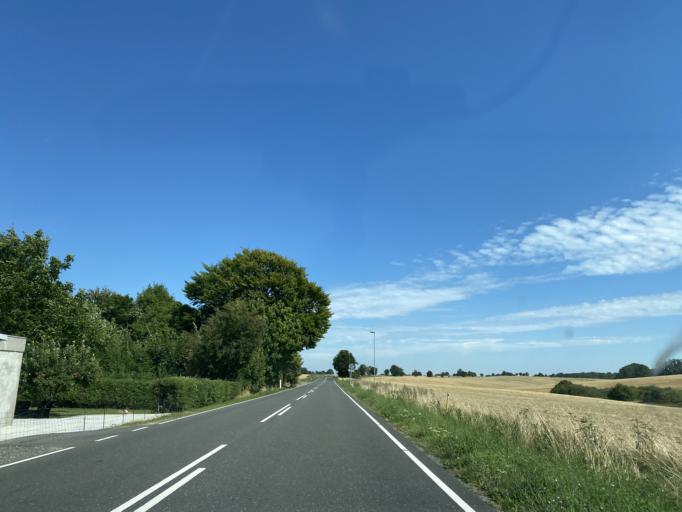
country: DK
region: South Denmark
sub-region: Kerteminde Kommune
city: Langeskov
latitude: 55.2492
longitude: 10.6149
